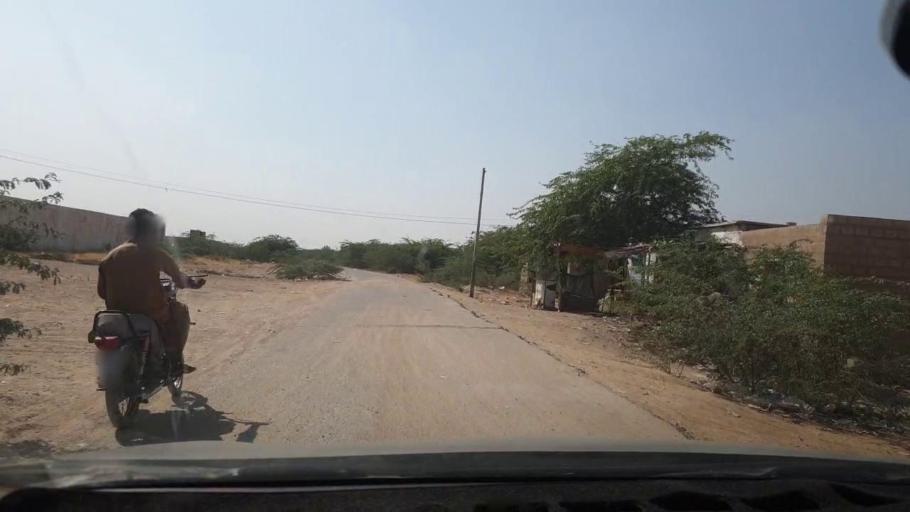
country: PK
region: Sindh
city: Malir Cantonment
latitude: 25.1281
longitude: 67.2261
